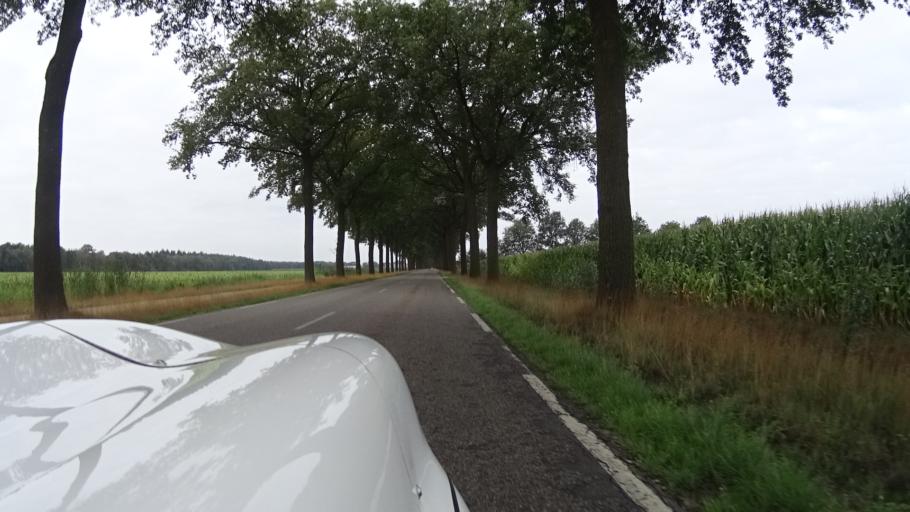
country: NL
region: North Brabant
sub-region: Gemeente Mill en Sint Hubert
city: Wilbertoord
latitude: 51.6292
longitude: 5.8140
